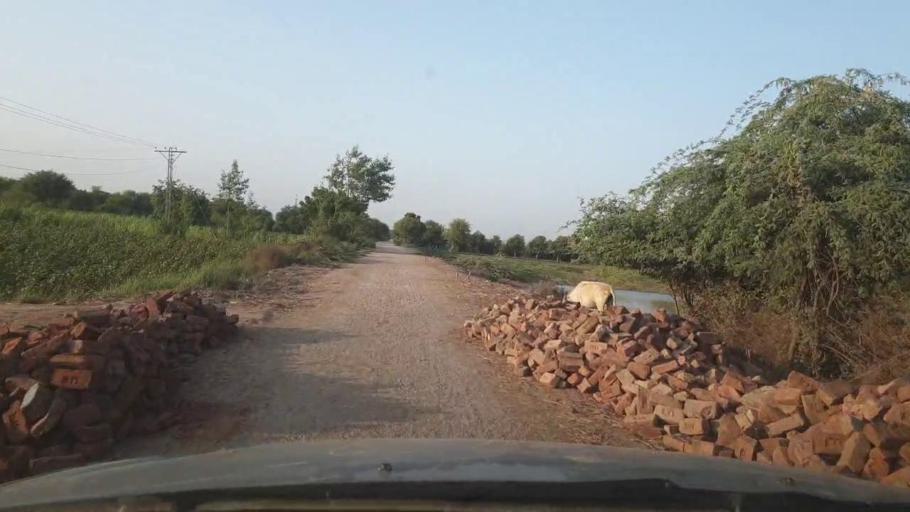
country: PK
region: Sindh
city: Tando Ghulam Ali
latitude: 25.1556
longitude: 68.9747
